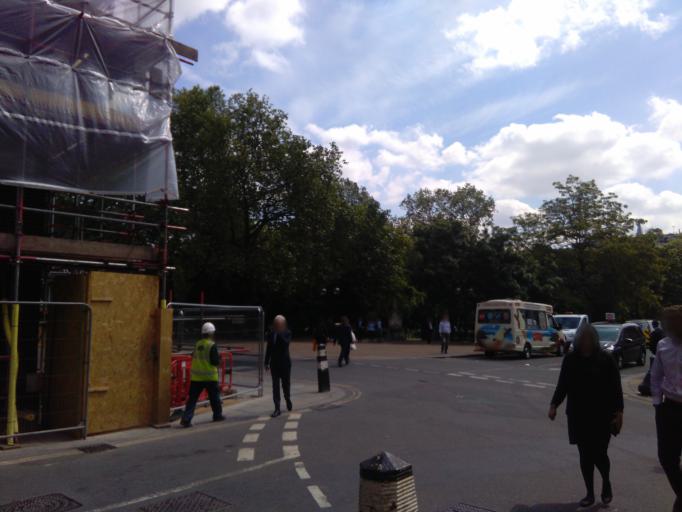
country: GB
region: England
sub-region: Greater London
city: London
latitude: 51.5170
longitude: -0.1190
